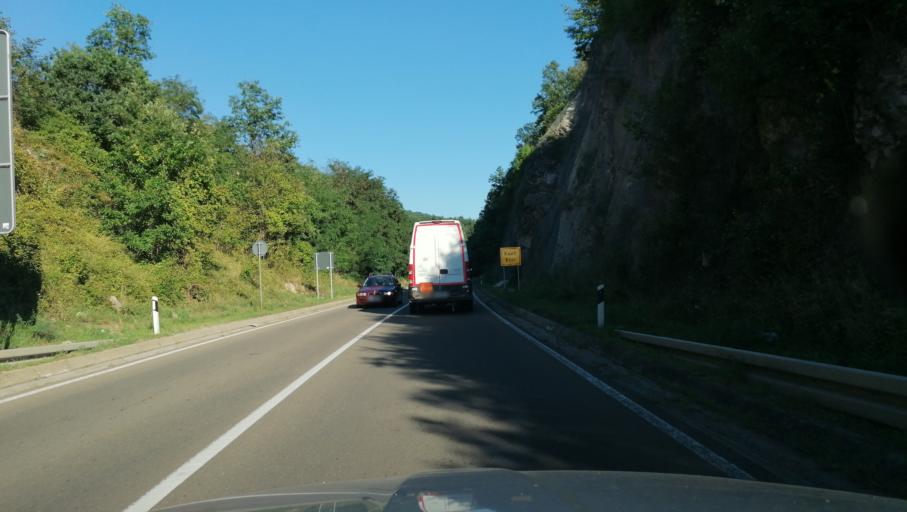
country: RS
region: Central Serbia
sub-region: Sumadijski Okrug
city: Knic
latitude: 43.9222
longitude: 20.6804
